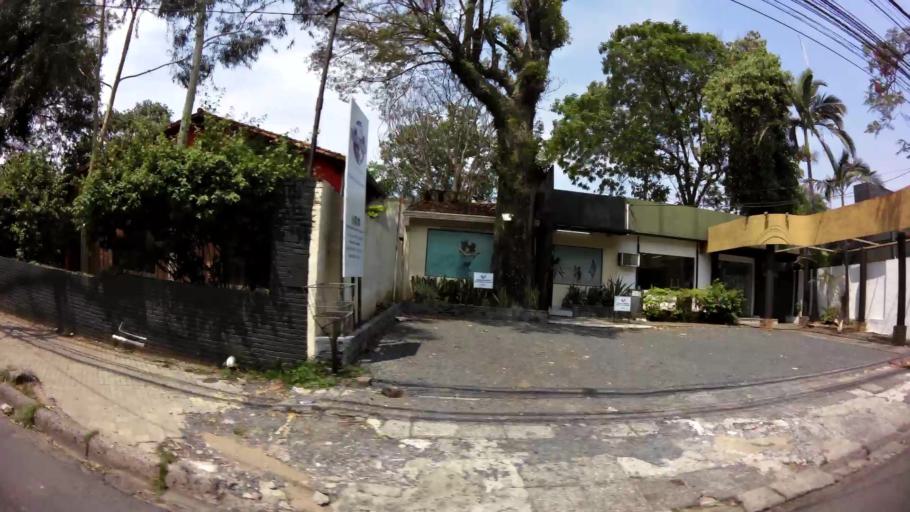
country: PY
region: Asuncion
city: Asuncion
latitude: -25.2861
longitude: -57.6095
